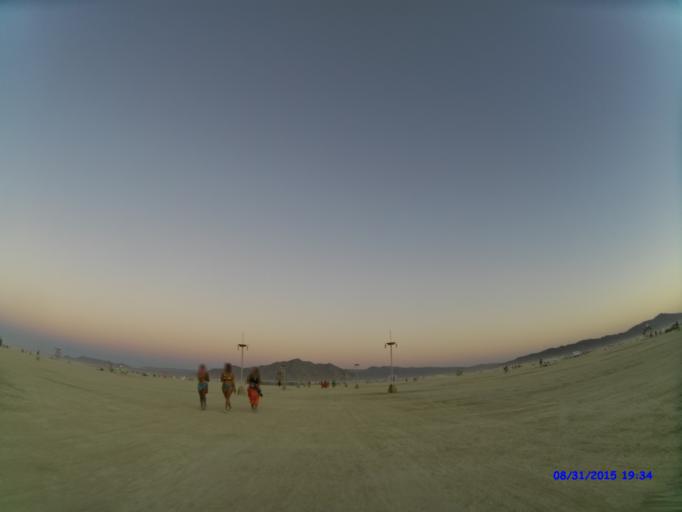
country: US
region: Nevada
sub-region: Pershing County
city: Lovelock
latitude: 40.7852
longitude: -119.2050
